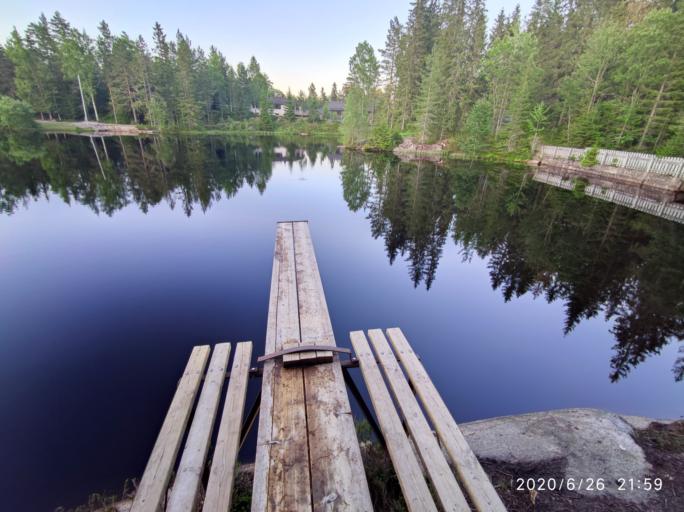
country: NO
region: Akershus
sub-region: Nannestad
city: Teigebyen
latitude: 60.1748
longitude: 10.9777
